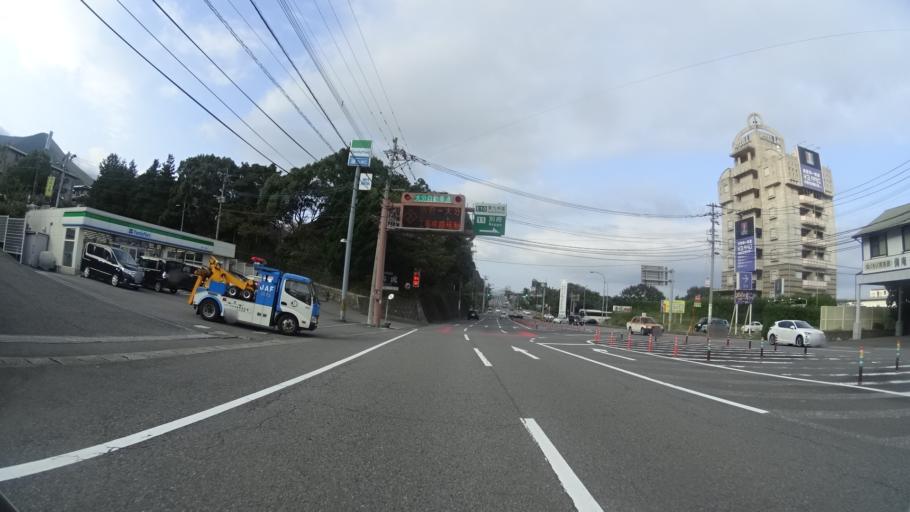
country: JP
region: Oita
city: Beppu
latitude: 33.2915
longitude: 131.4598
